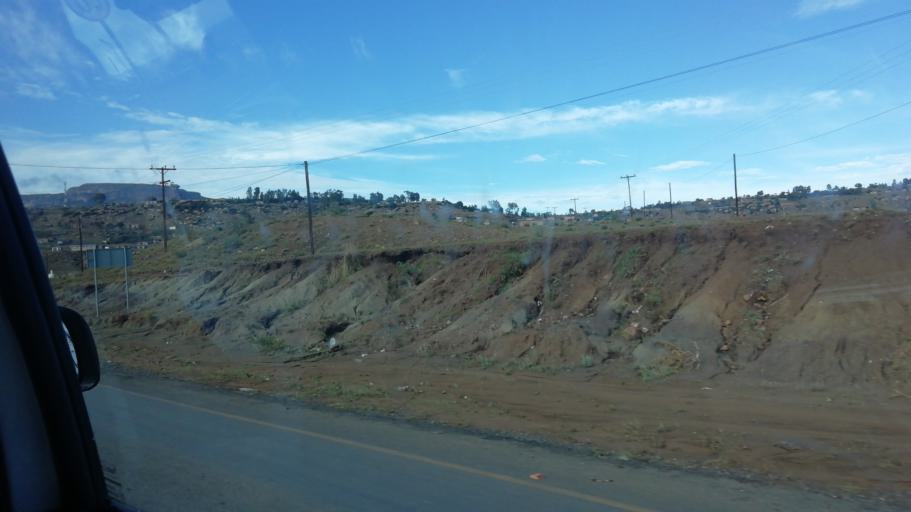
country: LS
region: Maseru
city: Maseru
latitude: -29.3868
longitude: 27.4705
